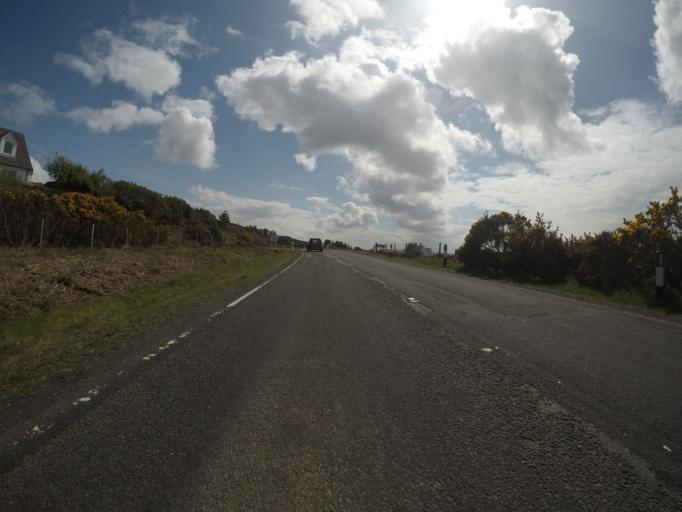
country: GB
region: Scotland
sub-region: Highland
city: Portree
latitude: 57.5739
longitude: -6.3652
